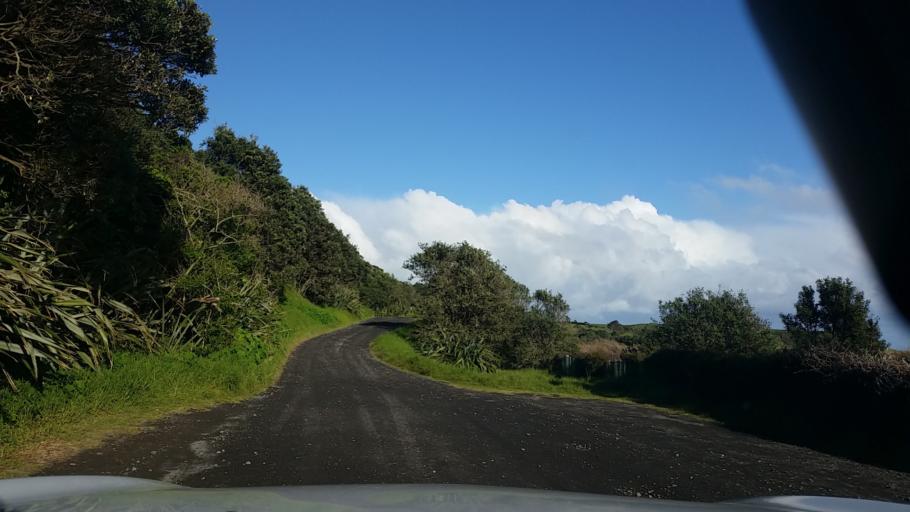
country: NZ
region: Taranaki
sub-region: New Plymouth District
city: New Plymouth
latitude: -39.1178
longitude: 173.9293
